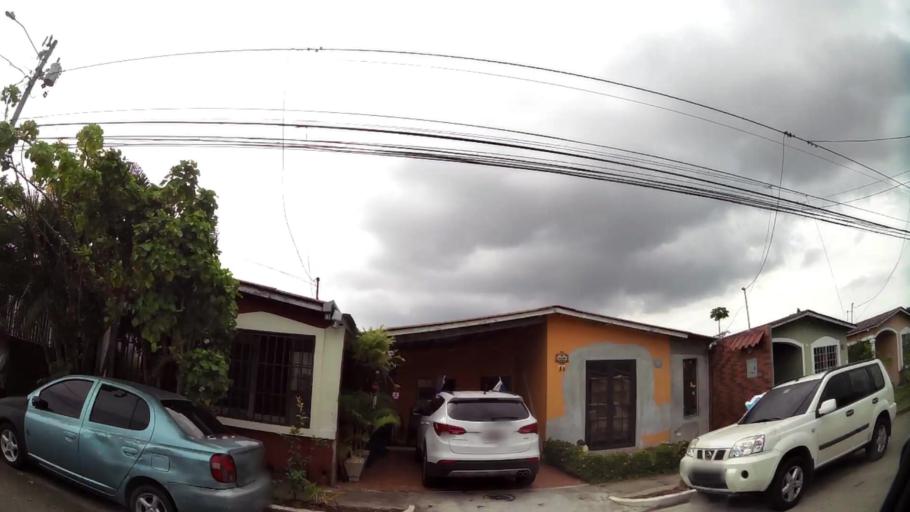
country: PA
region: Panama
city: Tocumen
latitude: 9.0479
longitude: -79.4064
